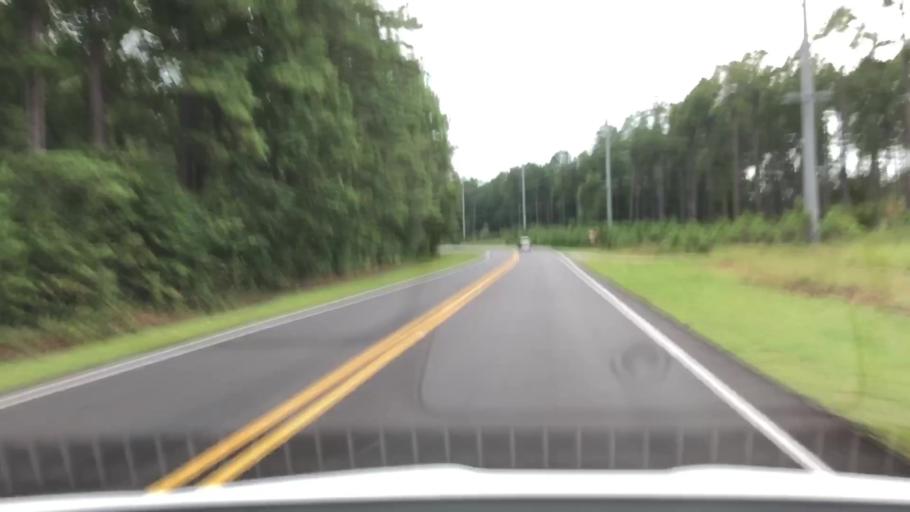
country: US
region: North Carolina
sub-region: Jones County
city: Maysville
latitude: 34.8203
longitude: -77.1479
